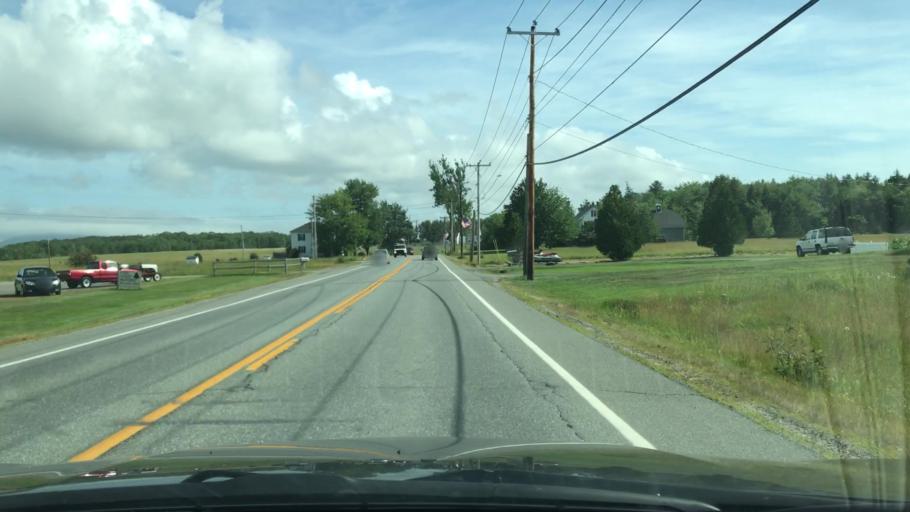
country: US
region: Maine
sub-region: Hancock County
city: Trenton
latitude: 44.4616
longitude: -68.3616
